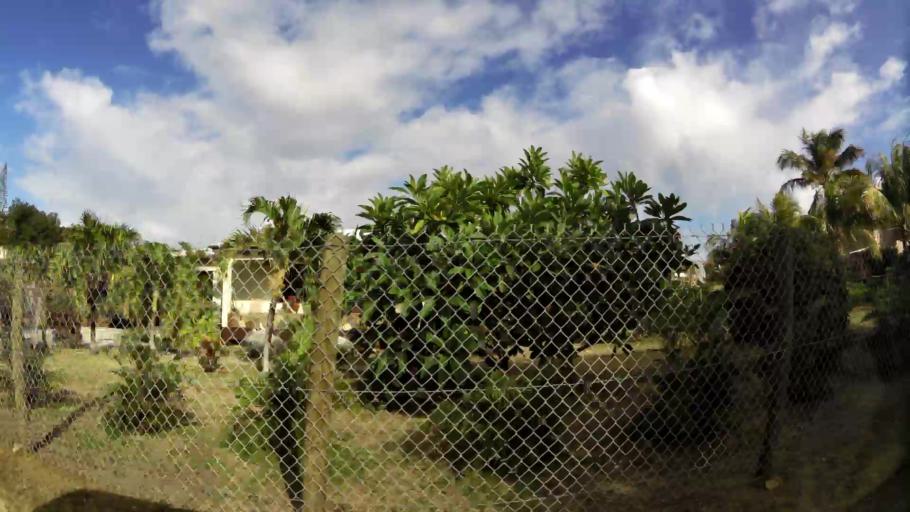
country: VG
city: Tortola
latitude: 18.4357
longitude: -64.4350
